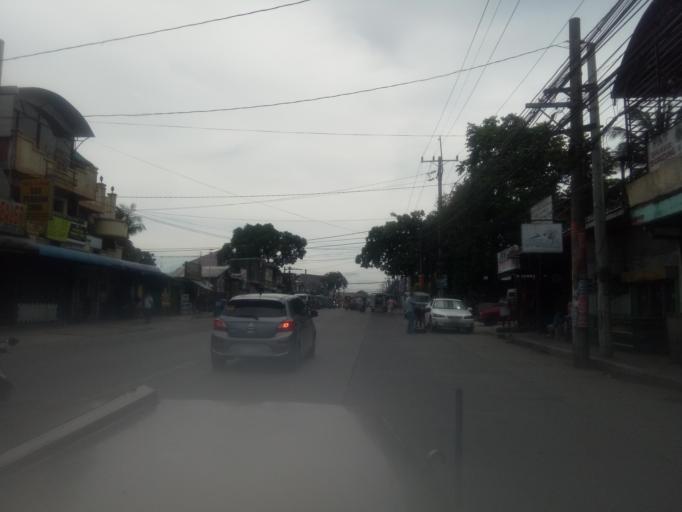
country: PH
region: Calabarzon
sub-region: Province of Cavite
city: Bulihan
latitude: 14.2878
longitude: 121.0018
